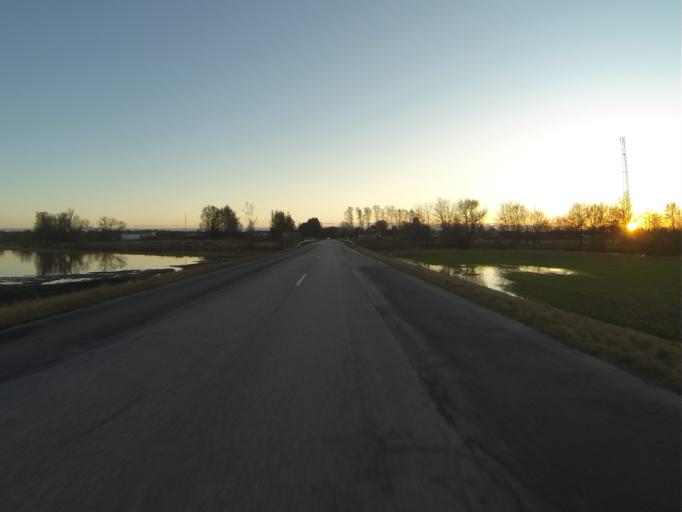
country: SE
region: Skane
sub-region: Hoors Kommun
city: Loberod
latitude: 55.7303
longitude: 13.4686
